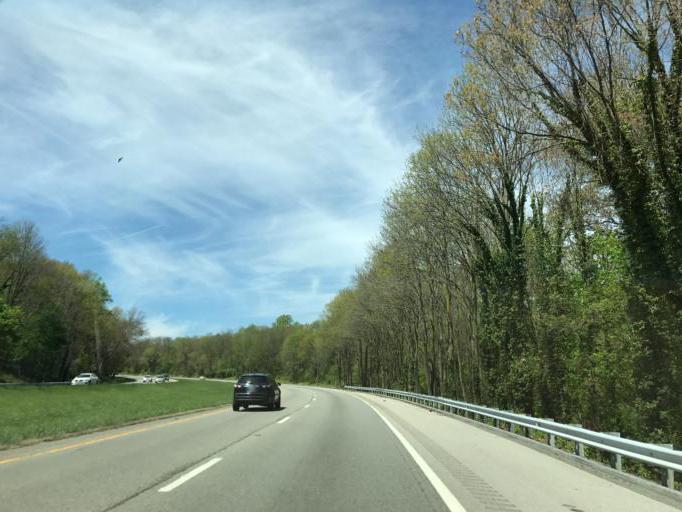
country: US
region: Delaware
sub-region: New Castle County
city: Claymont
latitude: 39.8045
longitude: -75.4736
